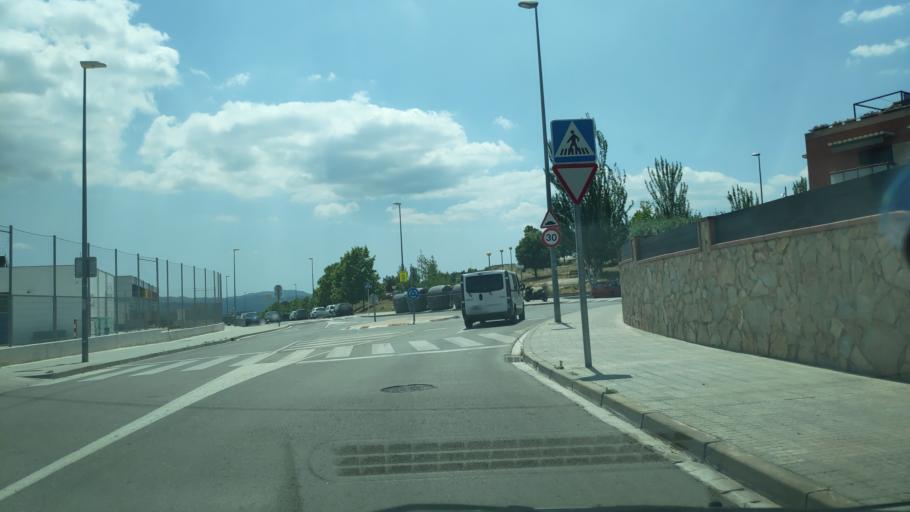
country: ES
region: Catalonia
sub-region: Provincia de Barcelona
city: Les Franqueses del Valles
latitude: 41.6189
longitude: 2.3013
